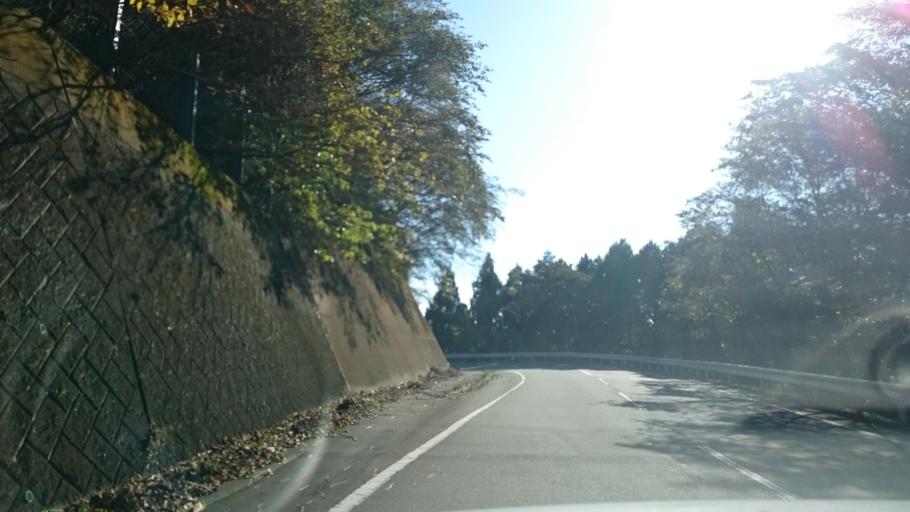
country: JP
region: Shizuoka
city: Heda
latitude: 34.9818
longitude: 138.8103
